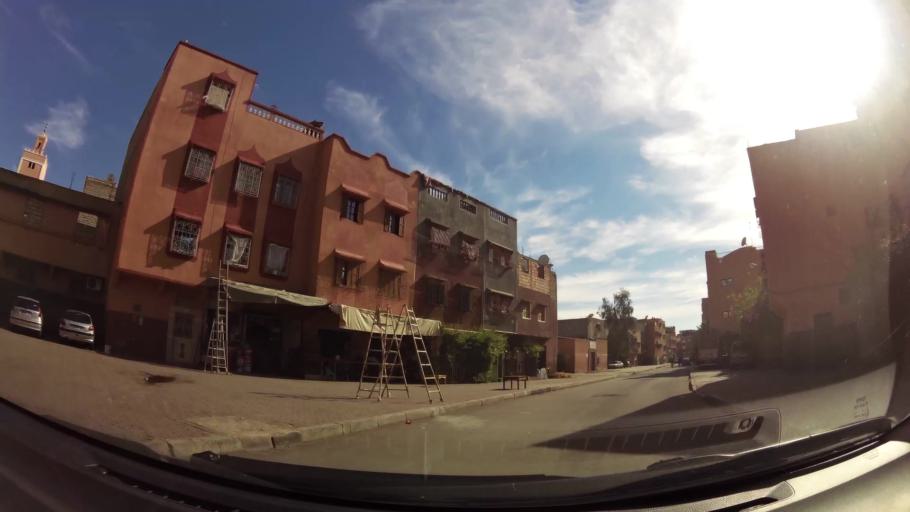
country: MA
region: Marrakech-Tensift-Al Haouz
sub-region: Marrakech
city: Marrakesh
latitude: 31.6069
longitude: -7.9604
